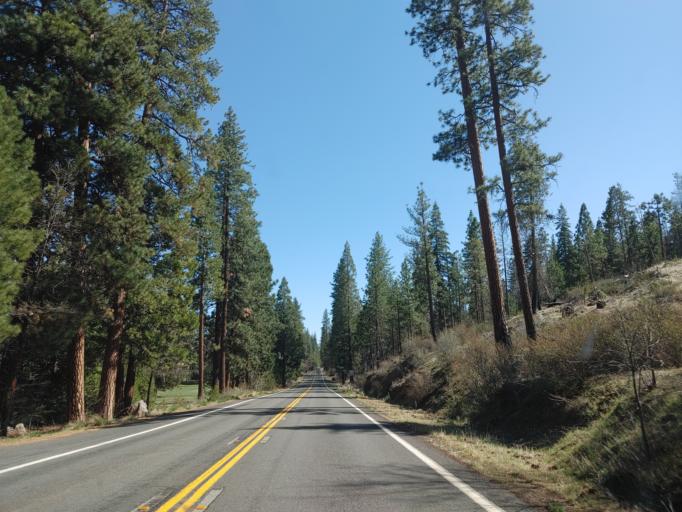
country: US
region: California
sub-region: Shasta County
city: Burney
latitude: 40.7975
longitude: -121.5104
